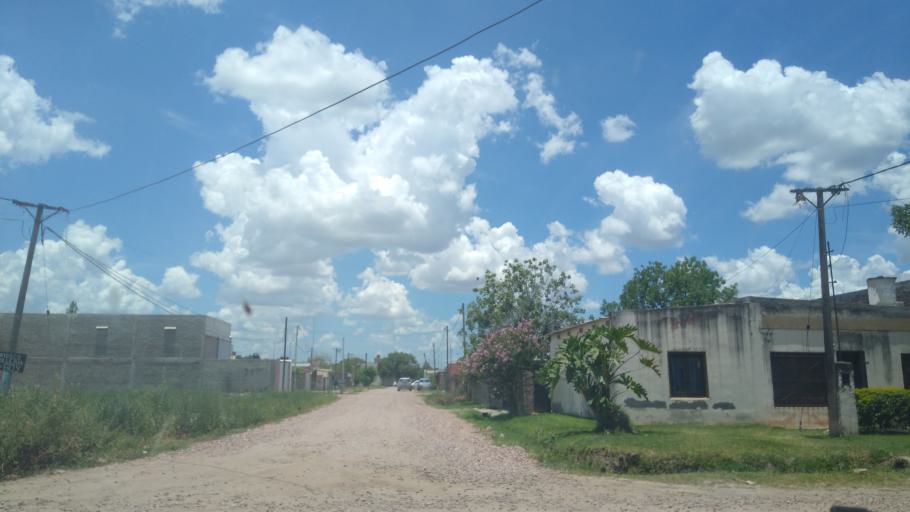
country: AR
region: Chaco
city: Presidencia Roque Saenz Pena
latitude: -26.7727
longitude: -60.4510
